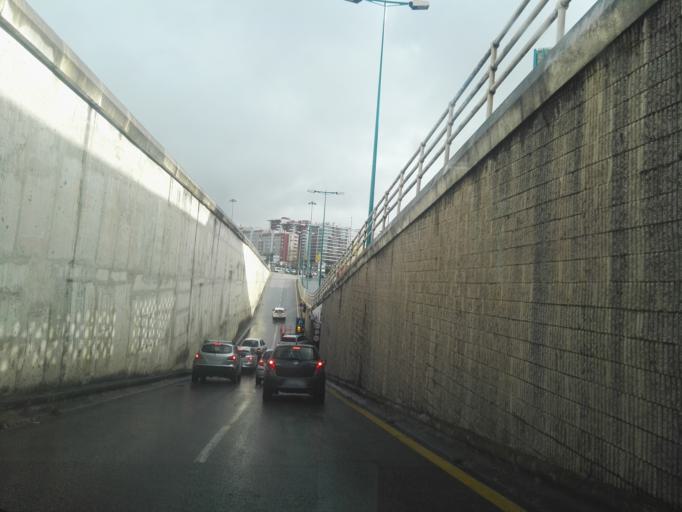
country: PT
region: Lisbon
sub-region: Odivelas
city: Pontinha
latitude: 38.7559
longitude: -9.1878
